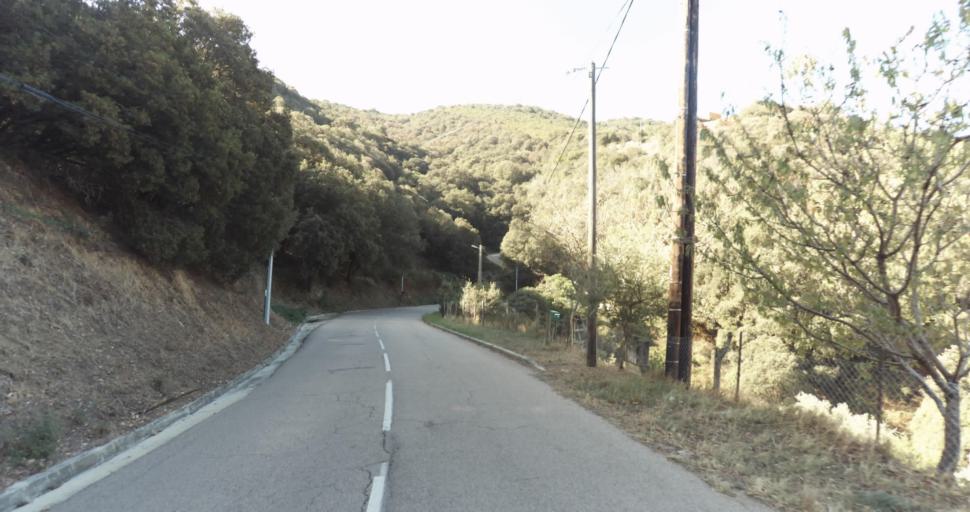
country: FR
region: Corsica
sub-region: Departement de la Corse-du-Sud
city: Ajaccio
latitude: 41.9253
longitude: 8.7097
